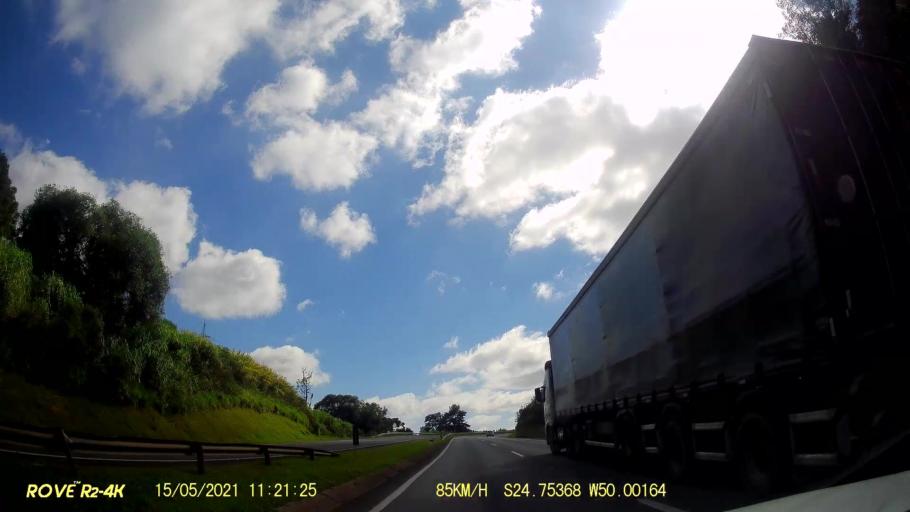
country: BR
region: Parana
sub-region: Castro
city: Castro
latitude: -24.7535
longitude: -50.0015
